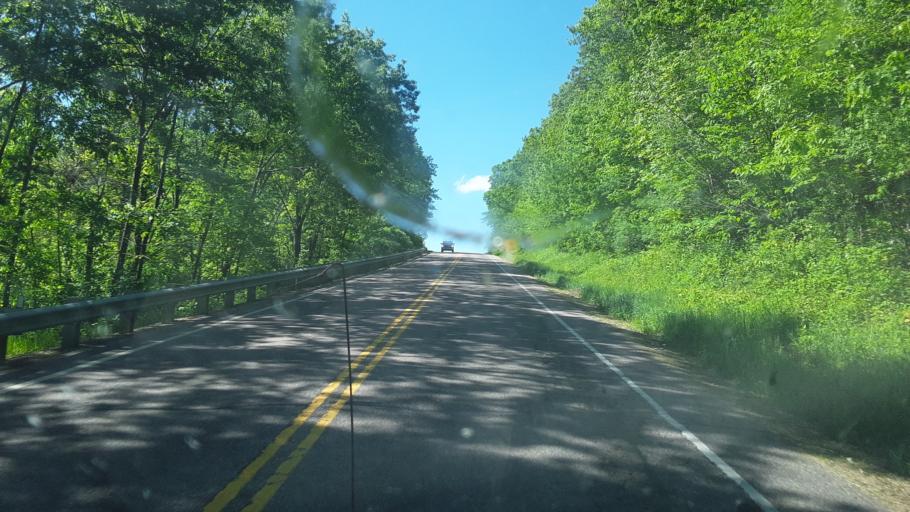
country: US
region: Wisconsin
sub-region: Sauk County
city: Reedsburg
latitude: 43.6181
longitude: -90.1209
